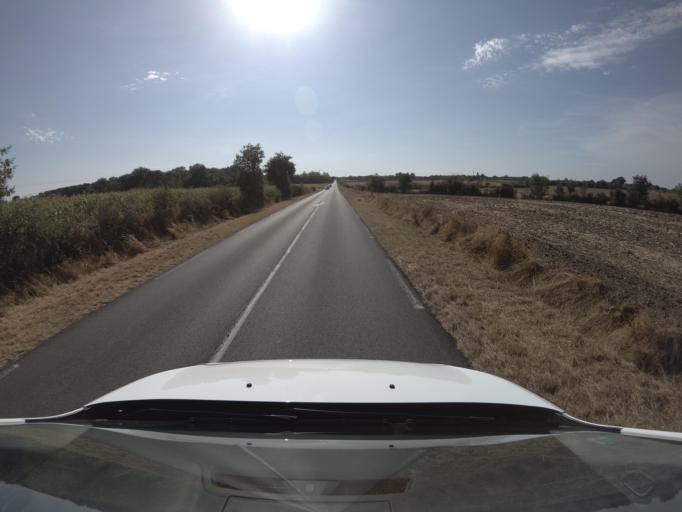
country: FR
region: Poitou-Charentes
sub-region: Departement des Deux-Sevres
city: Argenton-les-Vallees
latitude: 47.0012
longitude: -0.3840
